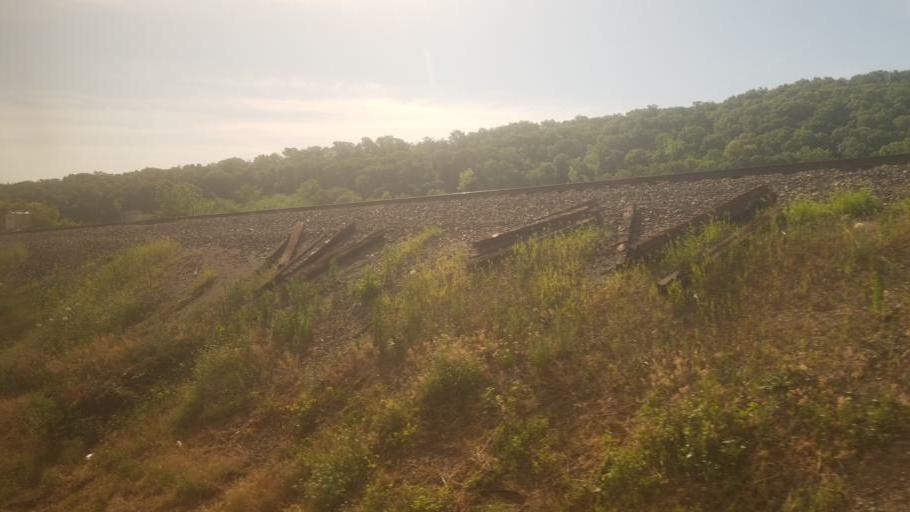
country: US
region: Kansas
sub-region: Johnson County
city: Shawnee
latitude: 39.0701
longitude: -94.7378
